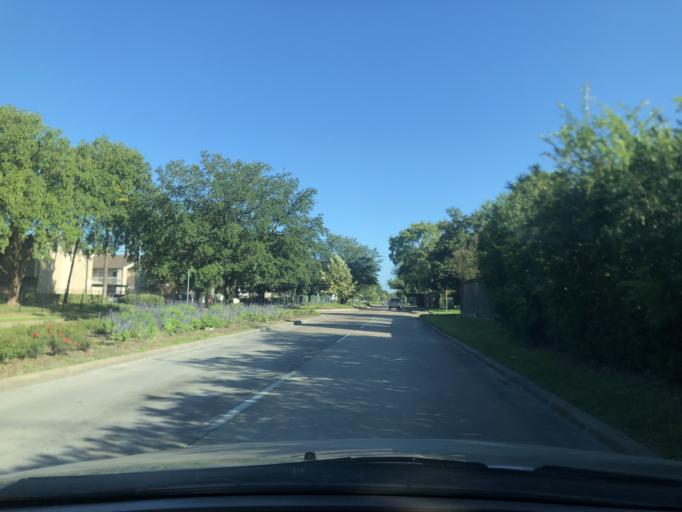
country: US
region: Texas
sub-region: Harris County
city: Bunker Hill Village
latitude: 29.7438
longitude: -95.5719
